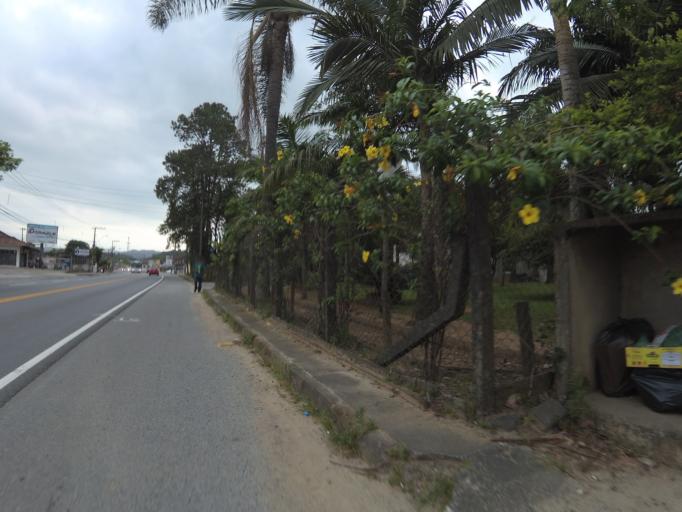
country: BR
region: Santa Catarina
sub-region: Blumenau
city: Blumenau
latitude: -26.8757
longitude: -49.1406
